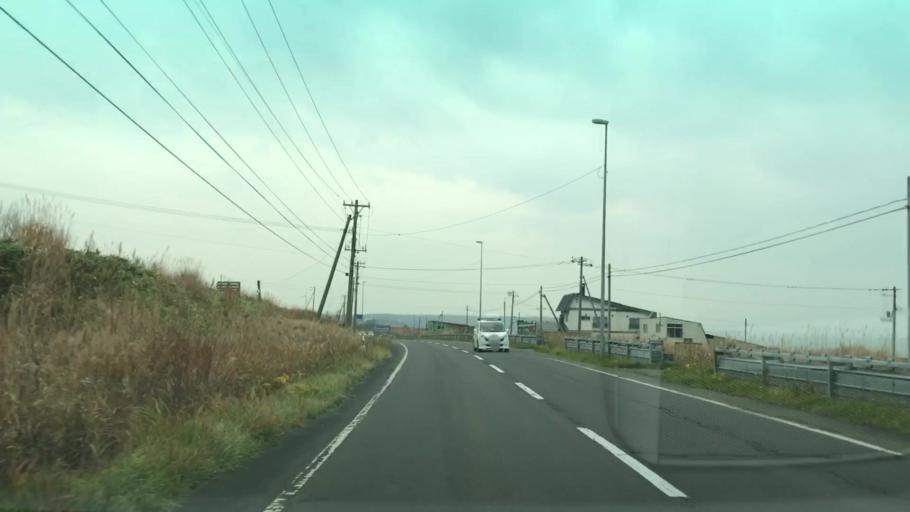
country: JP
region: Hokkaido
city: Ishikari
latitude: 43.3436
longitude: 141.4236
